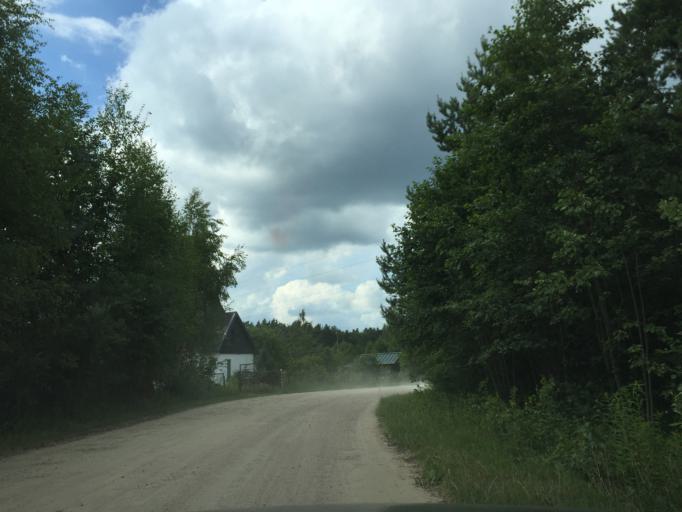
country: LV
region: Jelgava
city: Jelgava
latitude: 56.6270
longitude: 23.6239
